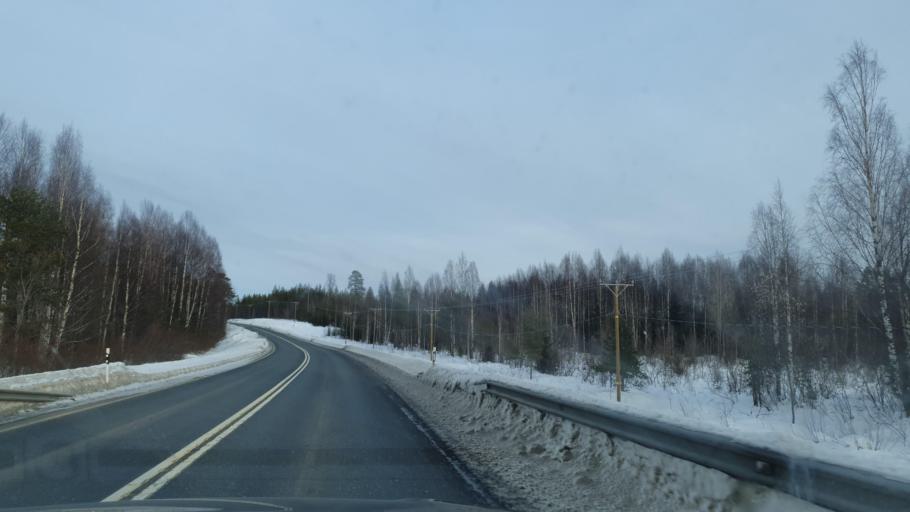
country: FI
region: North Karelia
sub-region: Pielisen Karjala
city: Valtimo
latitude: 64.0824
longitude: 29.0034
